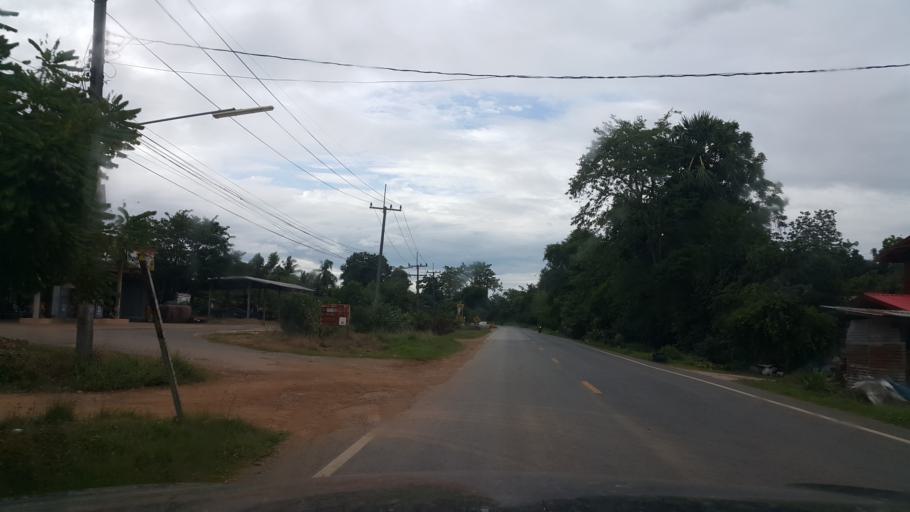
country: TH
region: Sukhothai
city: Ban Na
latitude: 17.0394
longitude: 99.7039
